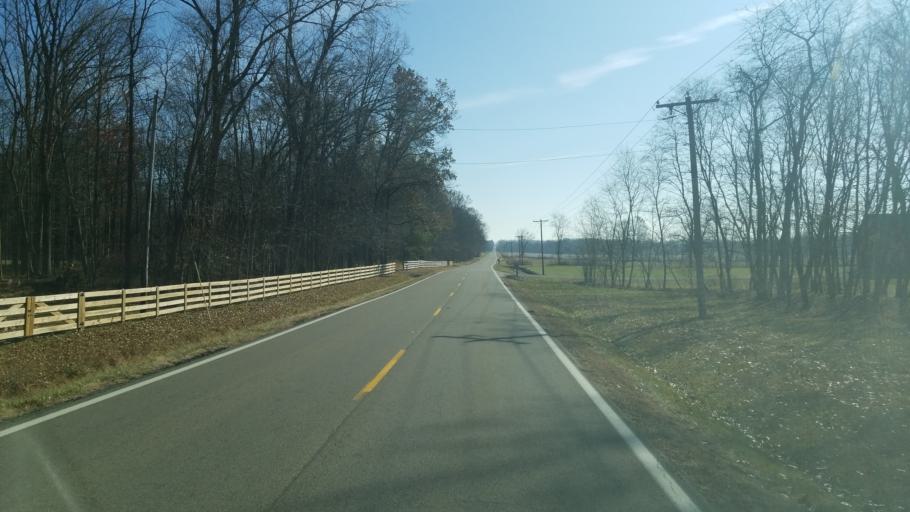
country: US
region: Ohio
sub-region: Licking County
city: Utica
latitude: 40.2009
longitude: -82.5308
